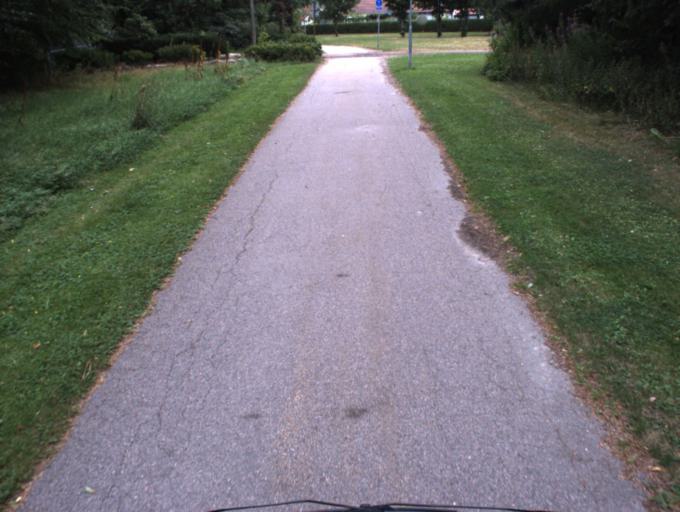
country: SE
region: Skane
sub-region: Helsingborg
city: Helsingborg
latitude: 56.0433
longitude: 12.7539
